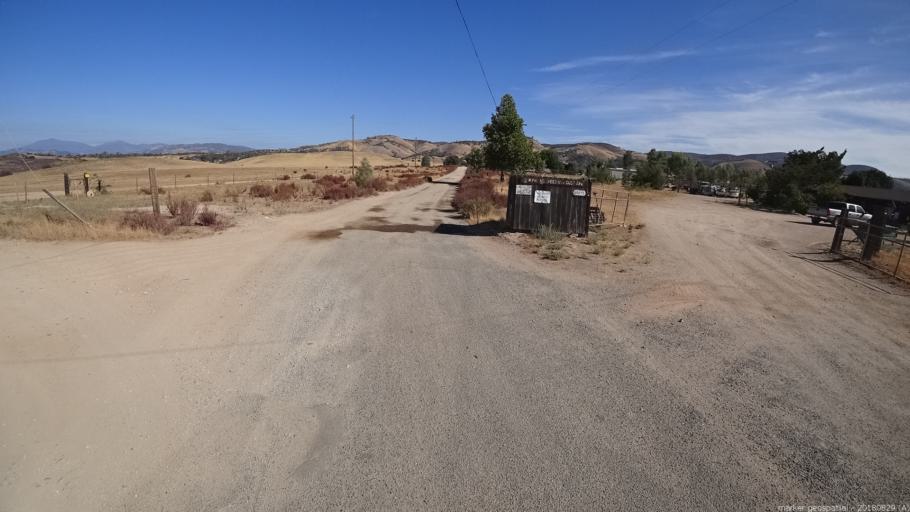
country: US
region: California
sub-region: Monterey County
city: King City
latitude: 35.9809
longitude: -121.1174
